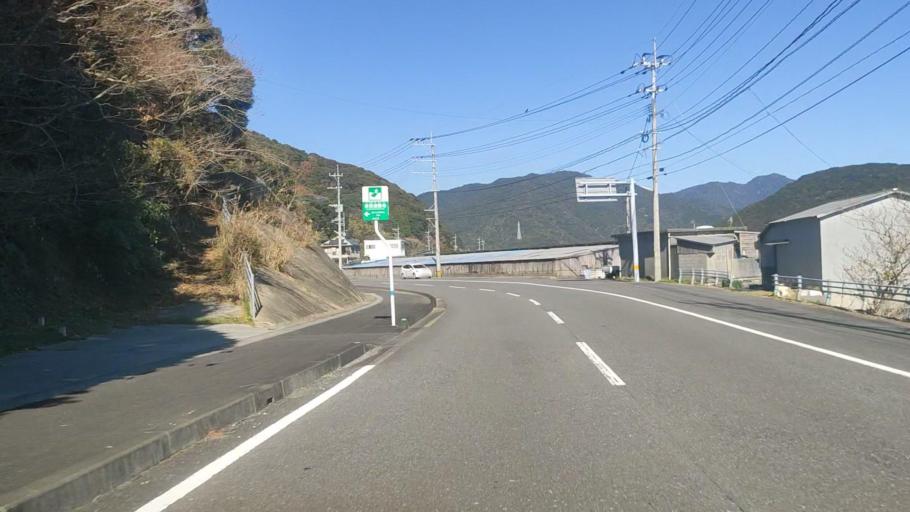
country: JP
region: Oita
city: Saiki
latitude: 32.8272
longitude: 131.9599
